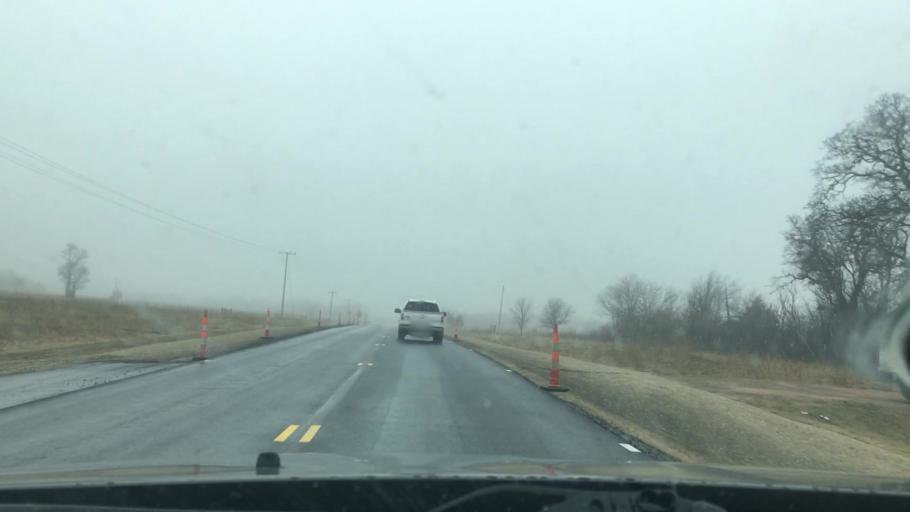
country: US
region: Oklahoma
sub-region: Johnston County
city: Tishomingo
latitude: 34.3171
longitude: -96.6710
